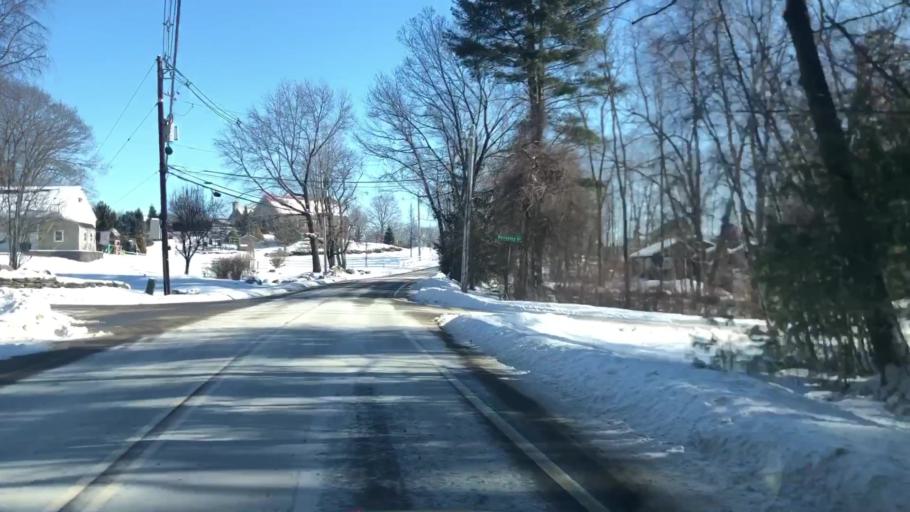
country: US
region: New Hampshire
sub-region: Hillsborough County
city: Bedford
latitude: 42.9421
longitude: -71.5433
